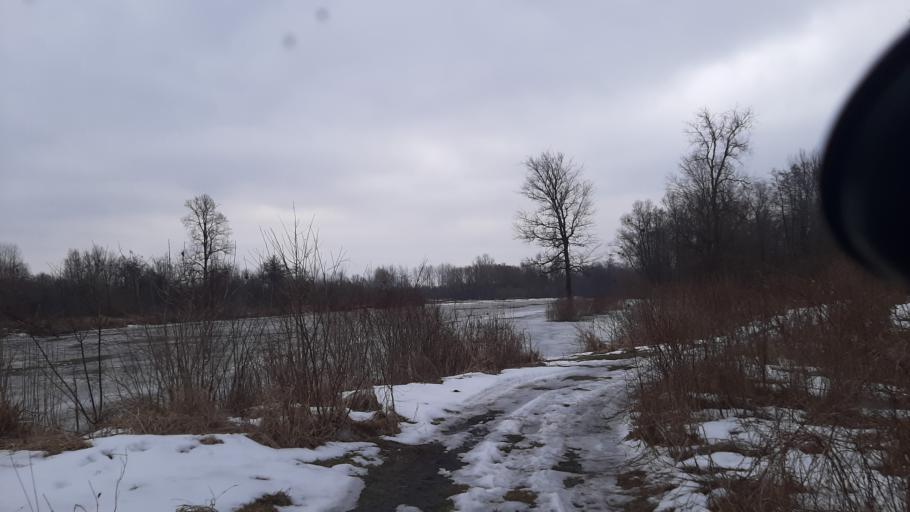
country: PL
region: Lublin Voivodeship
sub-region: Powiat wlodawski
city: Wlodawa
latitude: 51.5100
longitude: 23.6167
